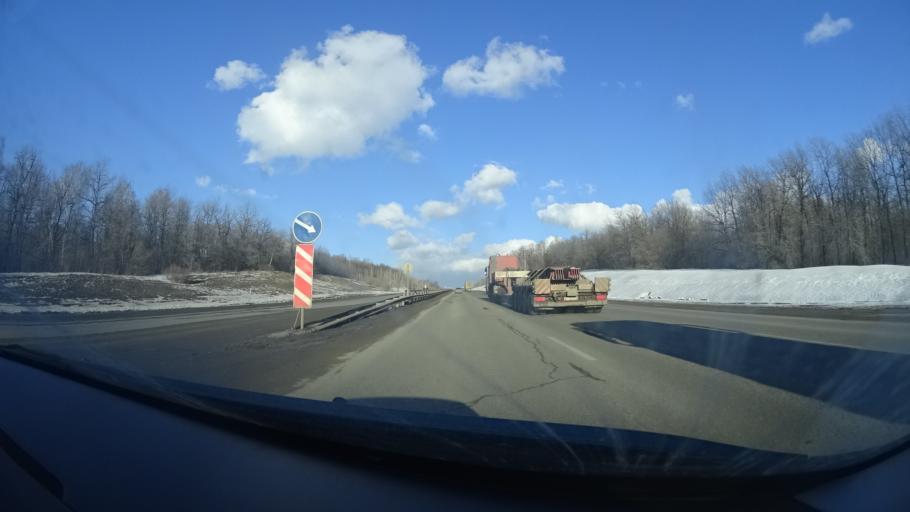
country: RU
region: Bashkortostan
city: Avdon
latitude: 54.6415
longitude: 55.6120
